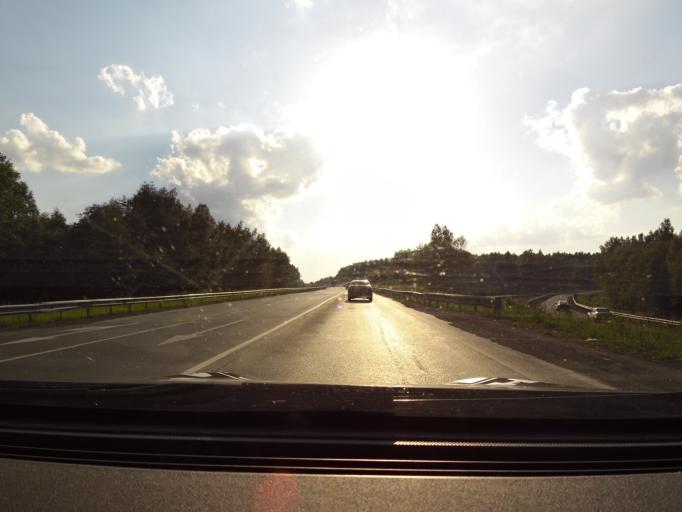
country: RU
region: Sverdlovsk
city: Talitsa
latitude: 56.8490
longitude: 60.0638
